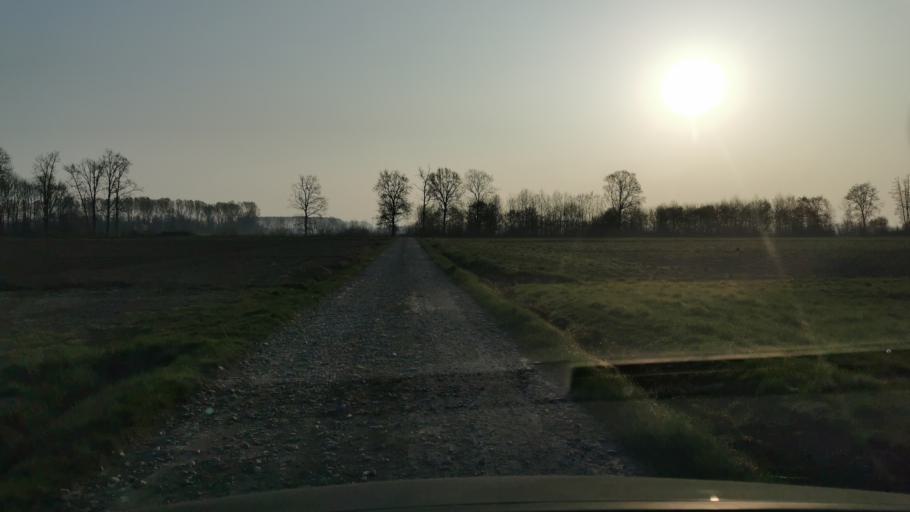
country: IT
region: Piedmont
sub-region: Provincia di Torino
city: Rivarossa
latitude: 45.2593
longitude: 7.7305
